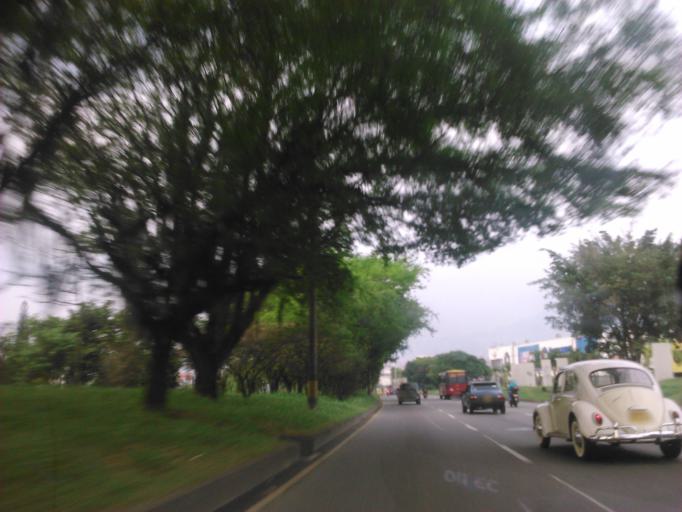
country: CO
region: Antioquia
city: Envigado
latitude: 6.1768
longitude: -75.5934
